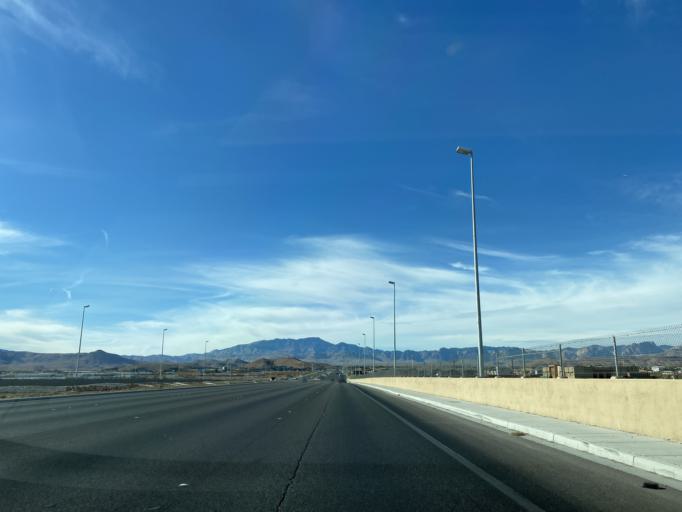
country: US
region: Nevada
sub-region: Clark County
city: Enterprise
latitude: 36.0254
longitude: -115.2280
